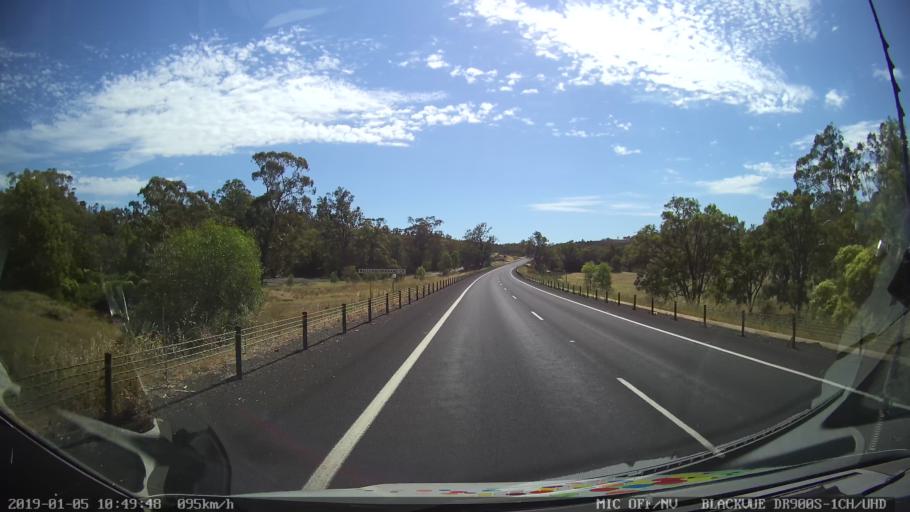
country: AU
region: New South Wales
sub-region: Warrumbungle Shire
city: Coonabarabran
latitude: -31.4315
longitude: 149.0660
